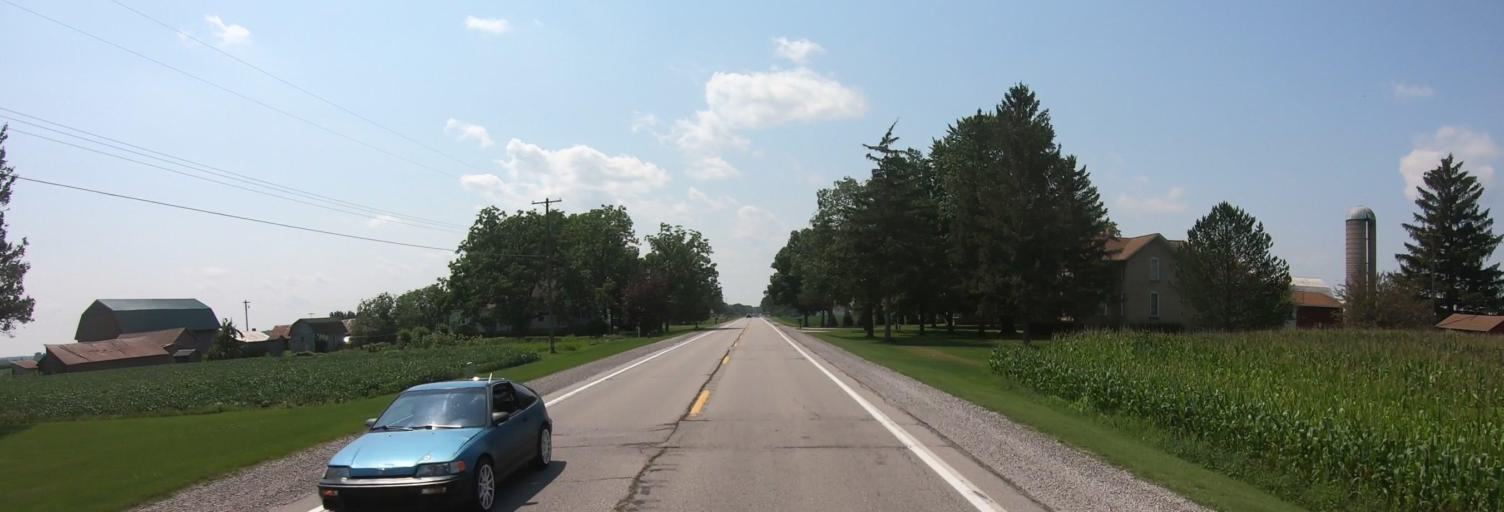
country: US
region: Michigan
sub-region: Saginaw County
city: Frankenmuth
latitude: 43.4072
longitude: -83.7939
